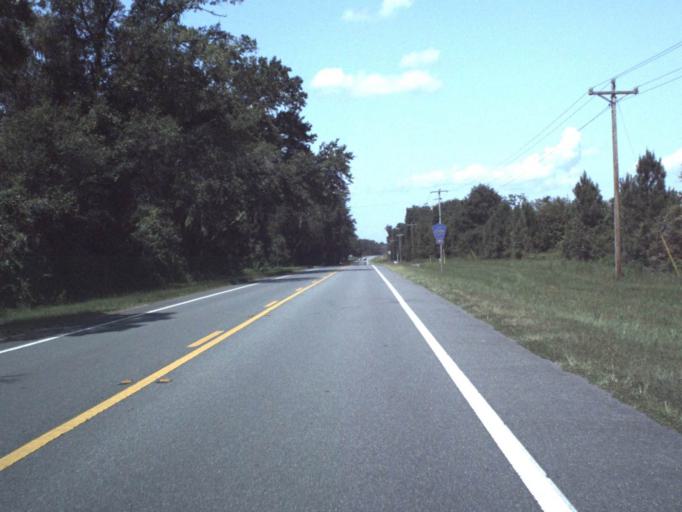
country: US
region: Florida
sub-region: Union County
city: Lake Butler
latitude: 30.0052
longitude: -82.4894
